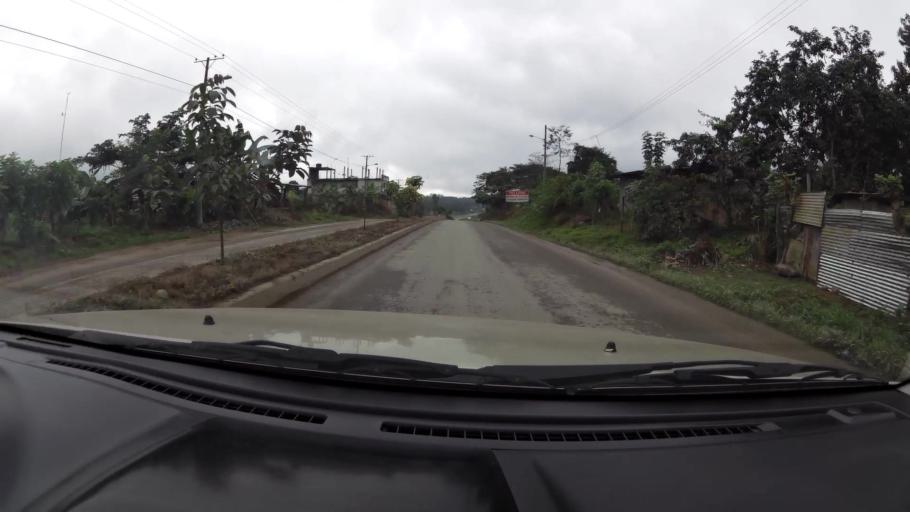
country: EC
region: El Oro
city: Pasaje
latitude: -3.3288
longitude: -79.7775
